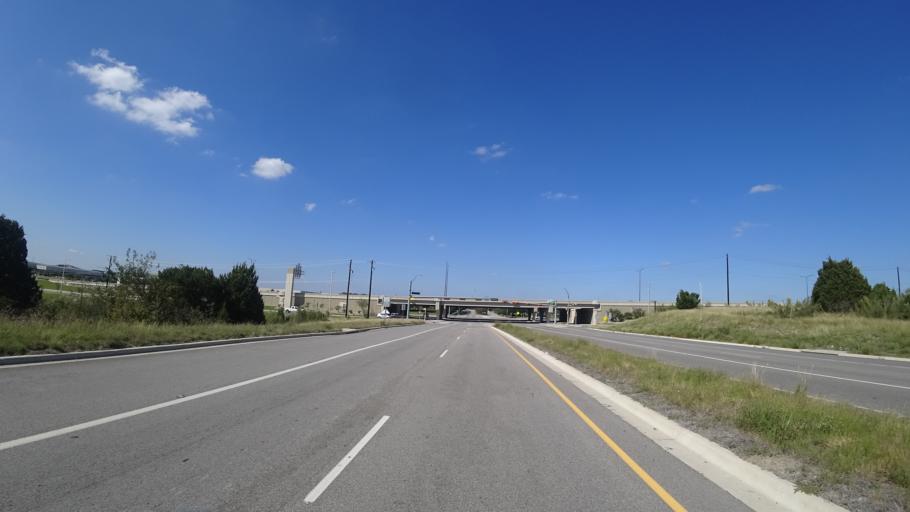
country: US
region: Texas
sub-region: Travis County
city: Manor
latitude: 30.3335
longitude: -97.6071
